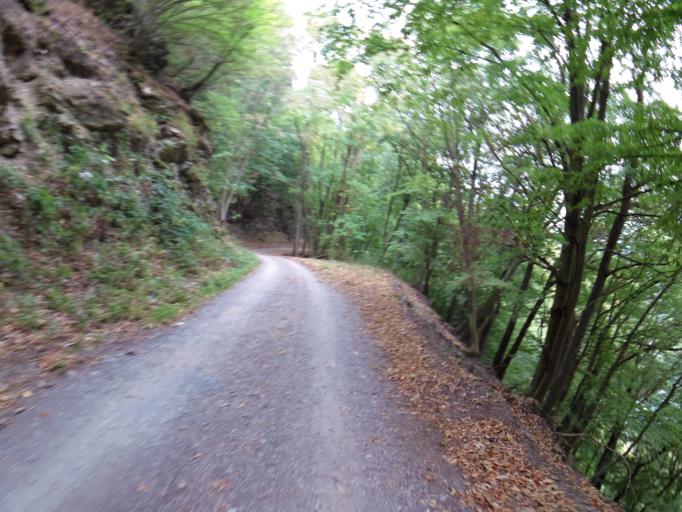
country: DE
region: North Rhine-Westphalia
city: Heimbach
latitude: 50.6261
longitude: 6.3990
